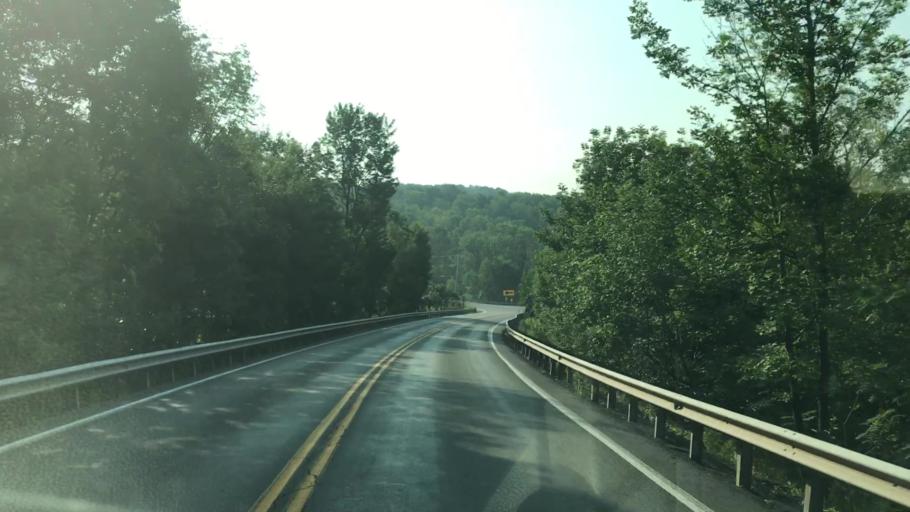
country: US
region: Pennsylvania
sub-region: Lackawanna County
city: Dalton
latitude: 41.5978
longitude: -75.6746
